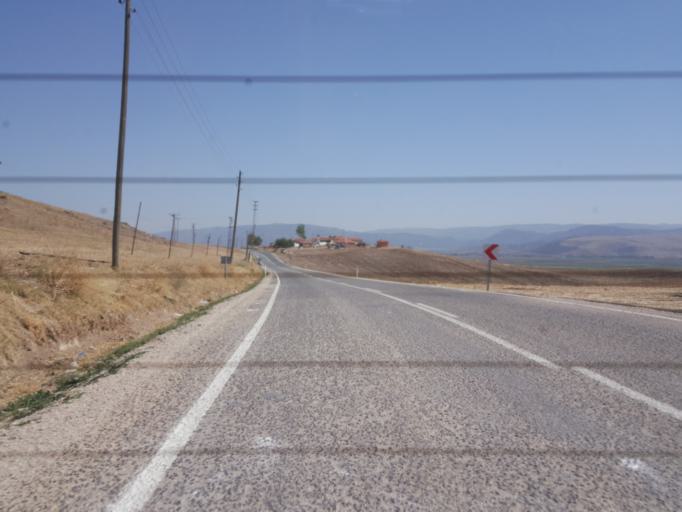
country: TR
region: Amasya
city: Dogantepe
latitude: 40.5833
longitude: 35.6283
